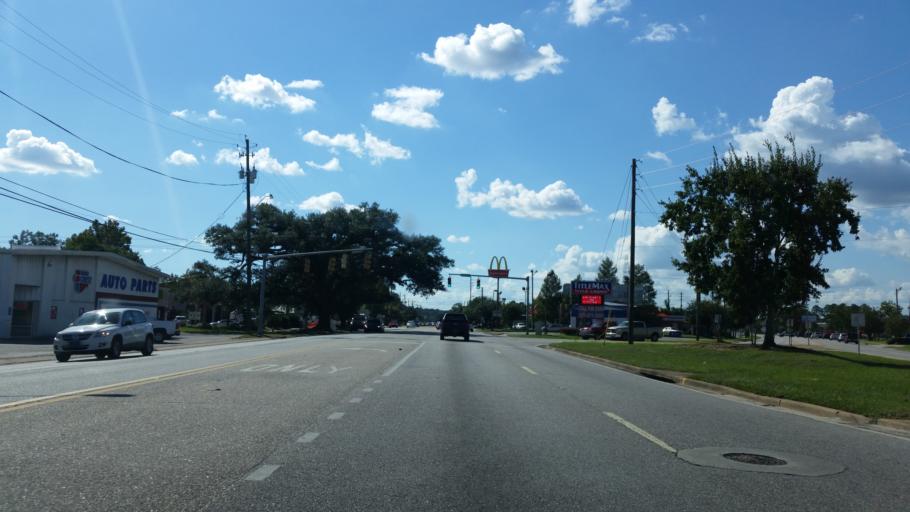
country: US
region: Alabama
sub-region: Mobile County
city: Prichard
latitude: 30.7006
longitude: -88.1133
